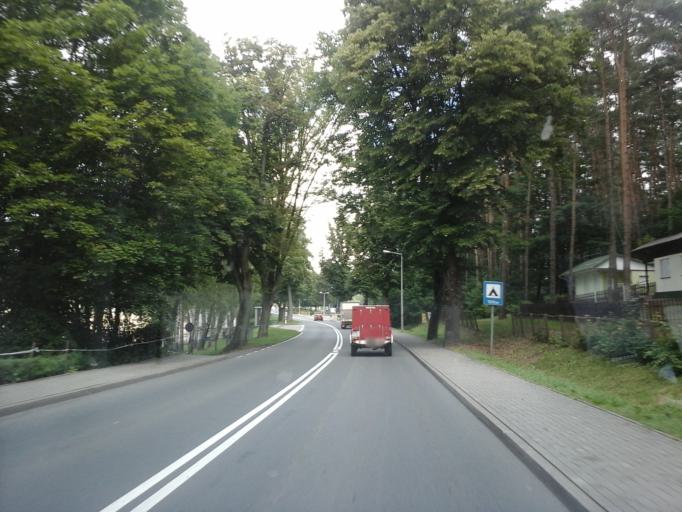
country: PL
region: Lubusz
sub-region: Powiat strzelecko-drezdenecki
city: Stare Kurowo
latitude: 52.9101
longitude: 15.6651
